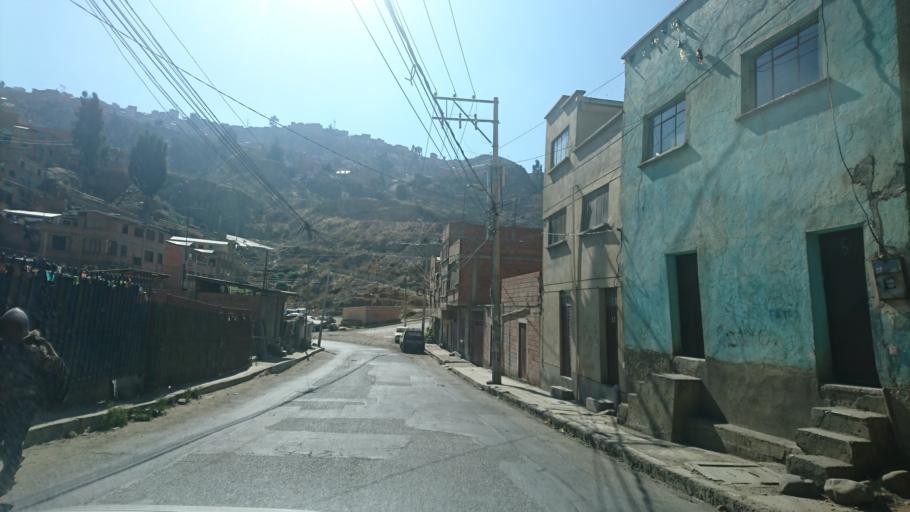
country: BO
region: La Paz
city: La Paz
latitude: -16.5068
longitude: -68.1119
